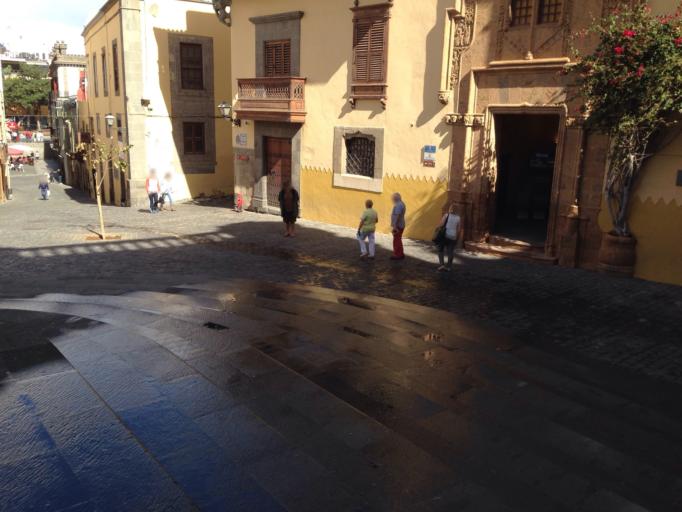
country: ES
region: Canary Islands
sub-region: Provincia de Las Palmas
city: Las Palmas de Gran Canaria
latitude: 28.1011
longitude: -15.4146
